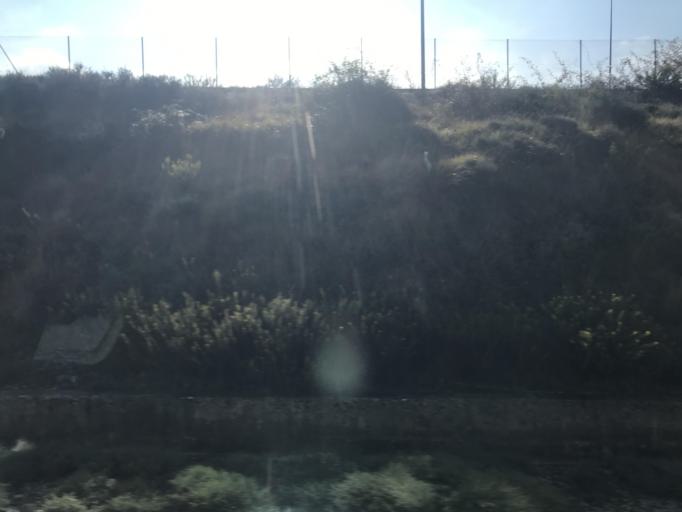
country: ES
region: Basque Country
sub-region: Provincia de Alava
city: Gasteiz / Vitoria
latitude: 42.8213
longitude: -2.7865
